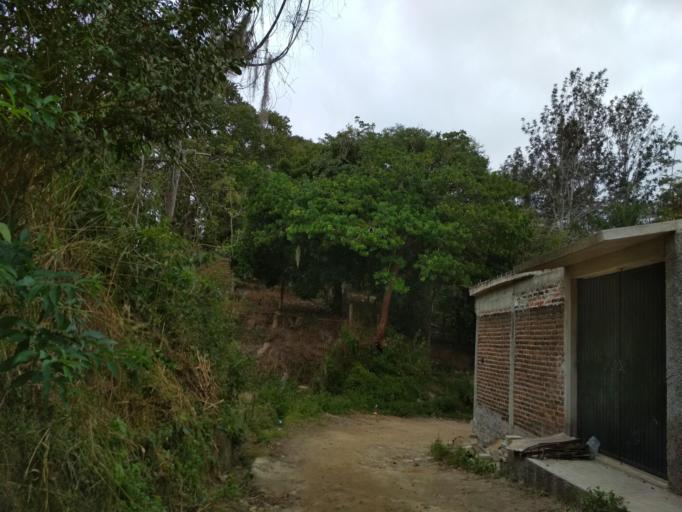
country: MX
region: Veracruz
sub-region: Emiliano Zapata
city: Dos Rios
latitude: 19.5364
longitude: -96.8014
